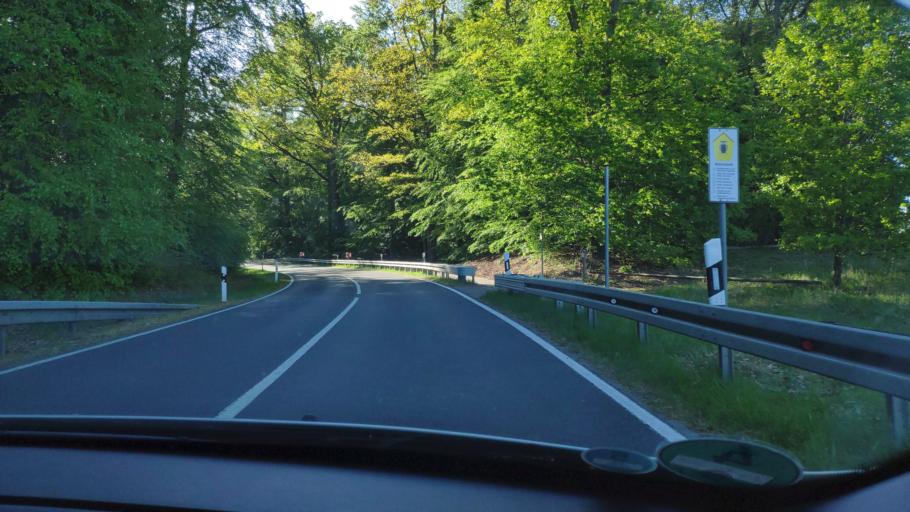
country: DE
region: Mecklenburg-Vorpommern
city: Wesenberg
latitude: 53.3208
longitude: 12.9594
